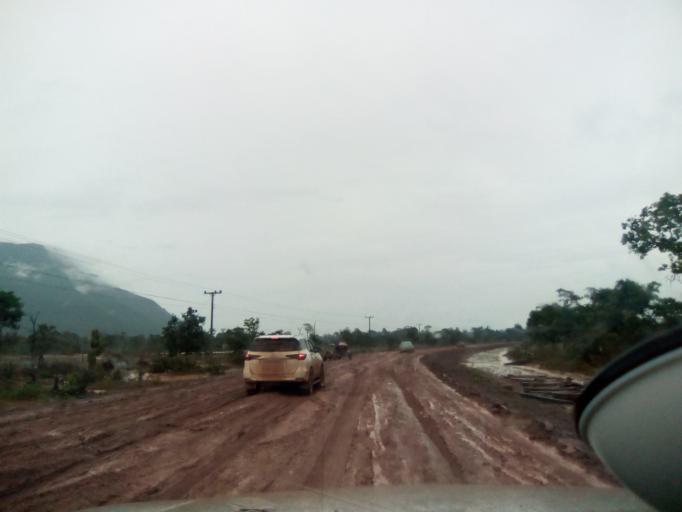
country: LA
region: Attapu
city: Attapu
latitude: 14.6903
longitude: 106.5399
